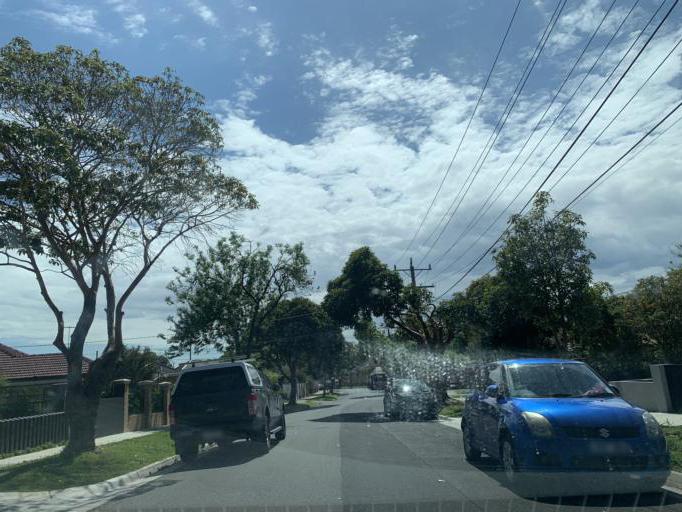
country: AU
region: Victoria
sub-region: Bayside
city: Hampton East
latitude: -37.9339
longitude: 145.0302
